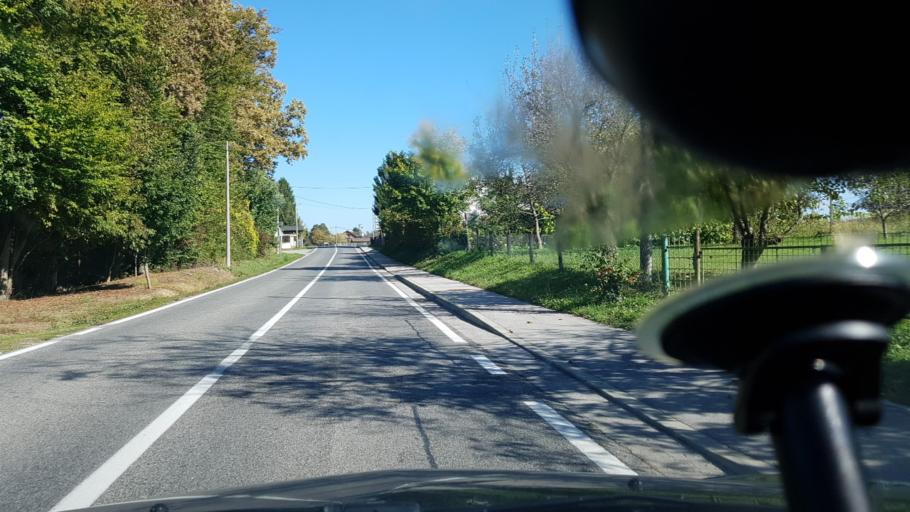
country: HR
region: Zagrebacka
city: Kriz
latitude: 45.7094
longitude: 16.4872
